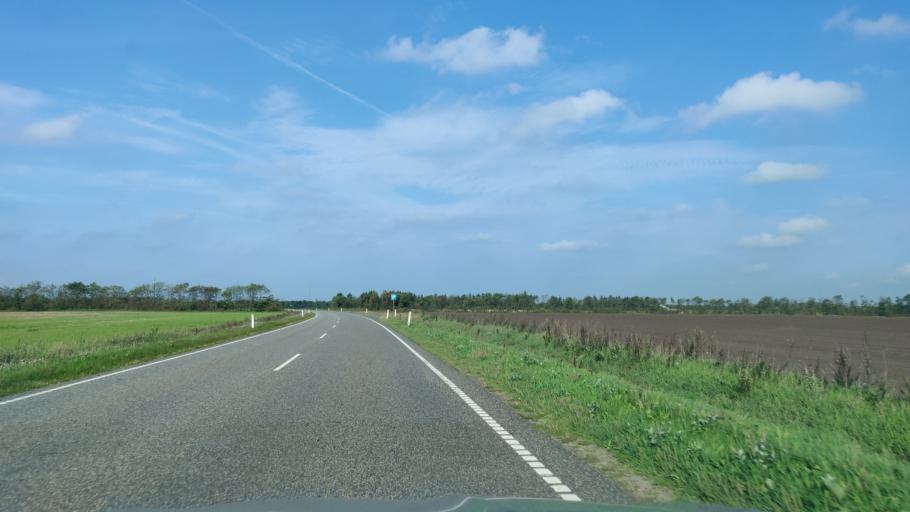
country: DK
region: Central Jutland
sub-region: Herning Kommune
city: Sunds
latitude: 56.2645
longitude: 9.0190
